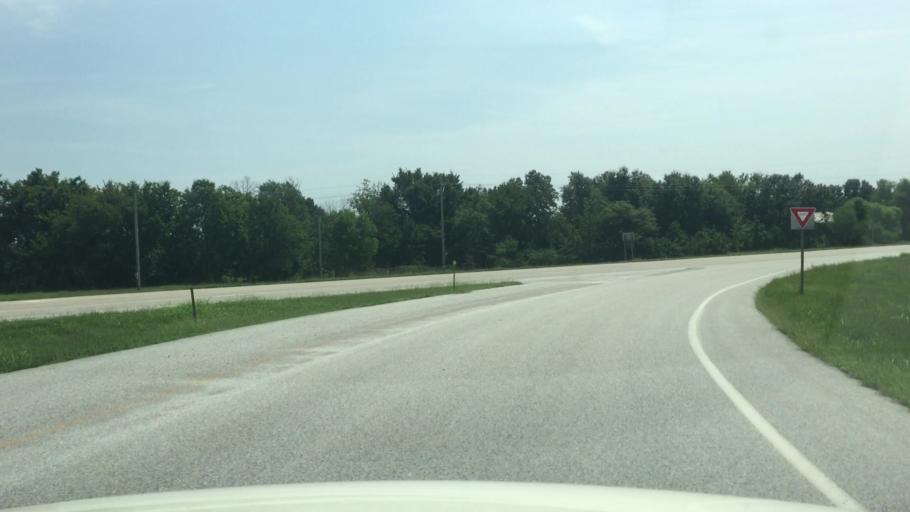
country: US
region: Kansas
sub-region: Cherokee County
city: Galena
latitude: 37.1773
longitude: -94.7050
